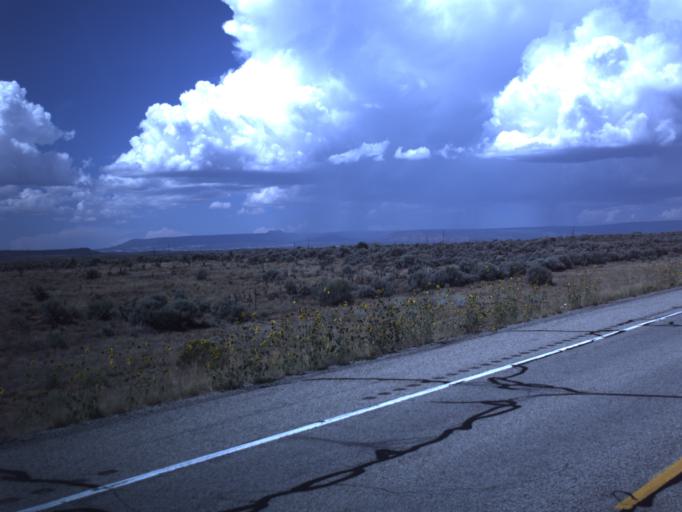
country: US
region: Utah
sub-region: San Juan County
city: Blanding
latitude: 37.5075
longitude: -109.4899
